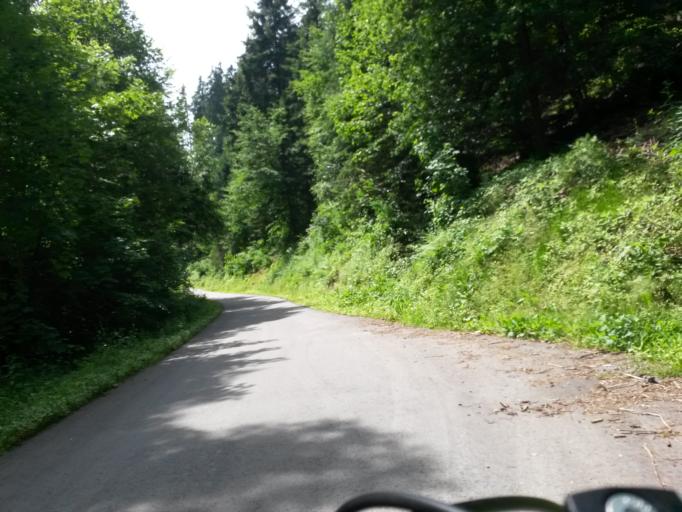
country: DE
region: Baden-Wuerttemberg
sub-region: Karlsruhe Region
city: Neubulach
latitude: 48.6624
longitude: 8.7251
